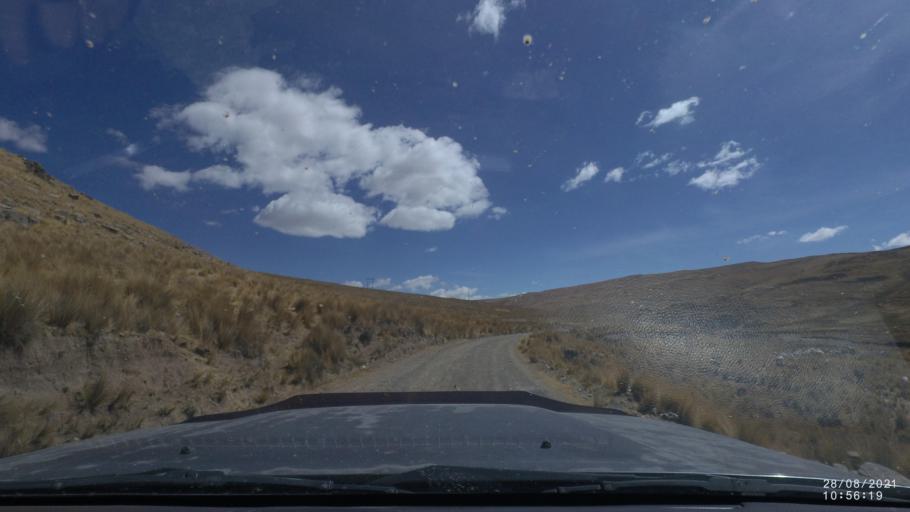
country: BO
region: Cochabamba
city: Cochabamba
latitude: -17.1939
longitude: -66.2496
